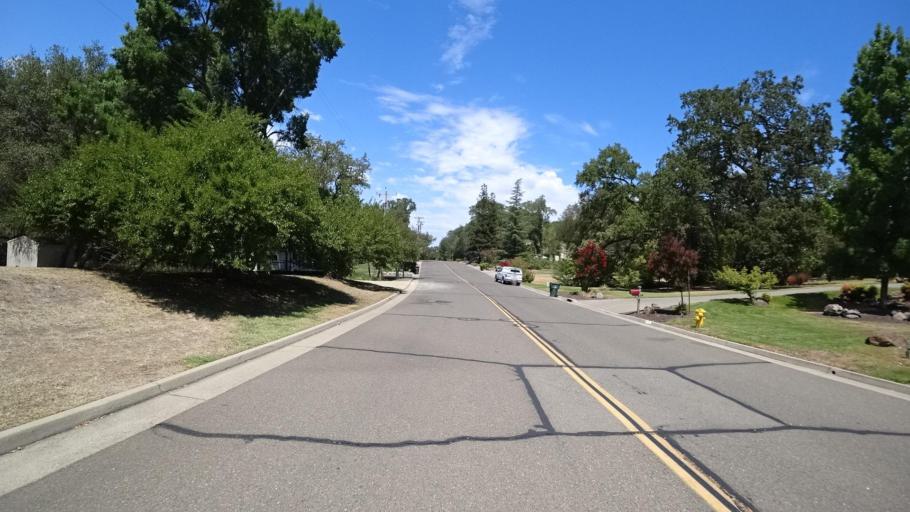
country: US
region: California
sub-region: Placer County
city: Rocklin
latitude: 38.8170
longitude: -121.2322
